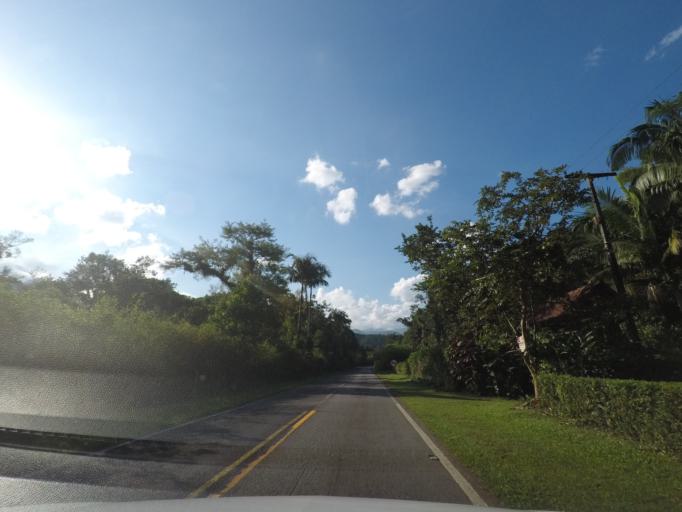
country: BR
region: Parana
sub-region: Antonina
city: Antonina
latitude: -25.4015
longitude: -48.8724
